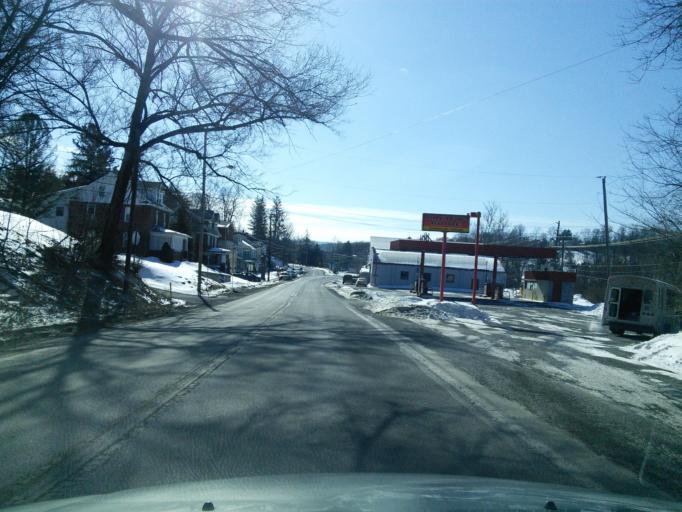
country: US
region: Pennsylvania
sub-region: Centre County
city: Bellefonte
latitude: 40.9176
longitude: -77.7855
